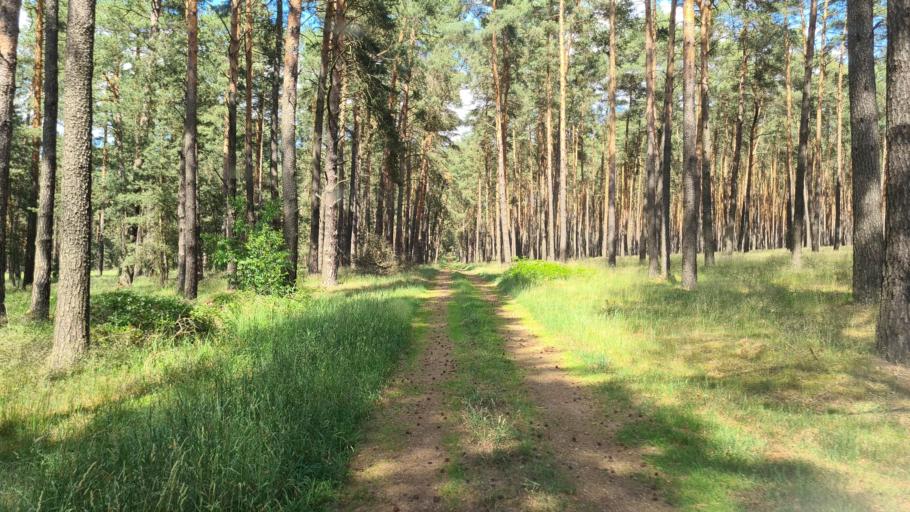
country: DE
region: Brandenburg
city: Sallgast
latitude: 51.6545
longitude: 13.8207
